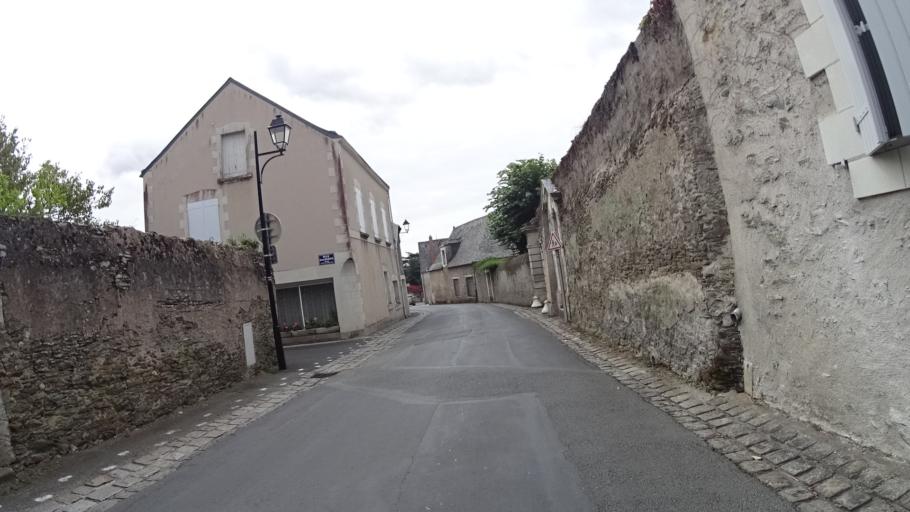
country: FR
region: Pays de la Loire
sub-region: Departement de Maine-et-Loire
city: Savennieres
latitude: 47.3835
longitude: -0.6600
